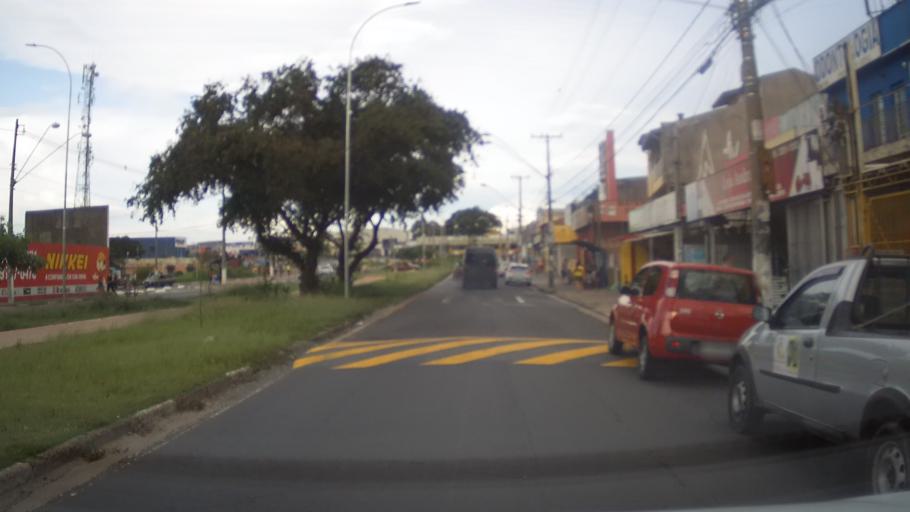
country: BR
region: Sao Paulo
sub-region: Hortolandia
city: Hortolandia
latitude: -22.9518
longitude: -47.1886
